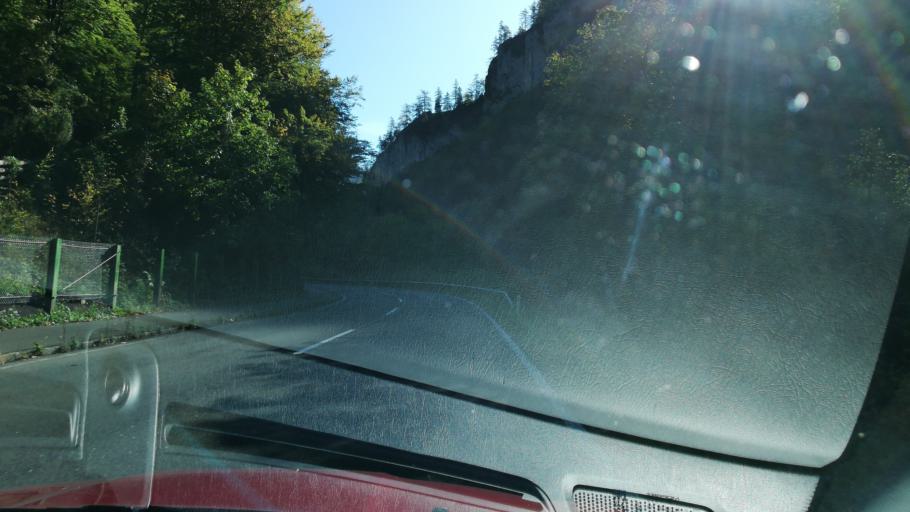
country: AT
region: Styria
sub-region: Politischer Bezirk Leoben
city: Hieflau
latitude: 47.5857
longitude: 14.8127
